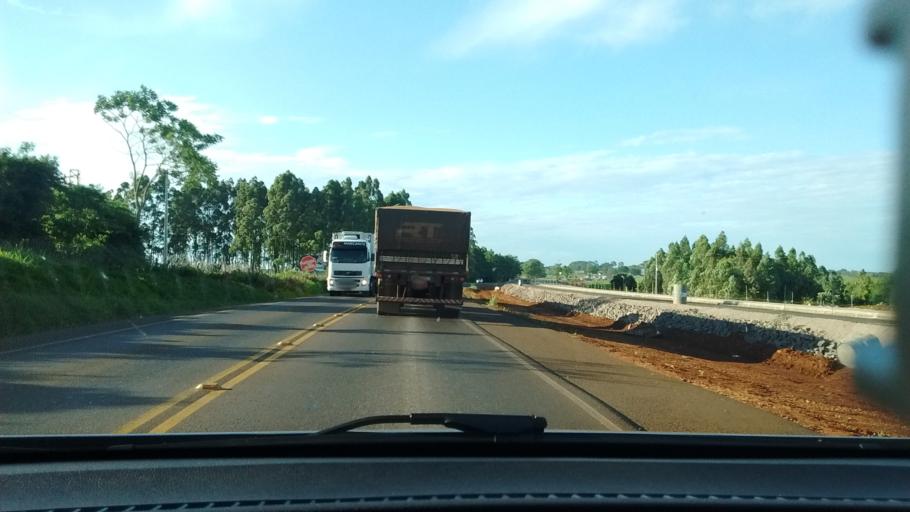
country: BR
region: Parana
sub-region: Cascavel
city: Cascavel
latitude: -25.1618
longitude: -53.5976
